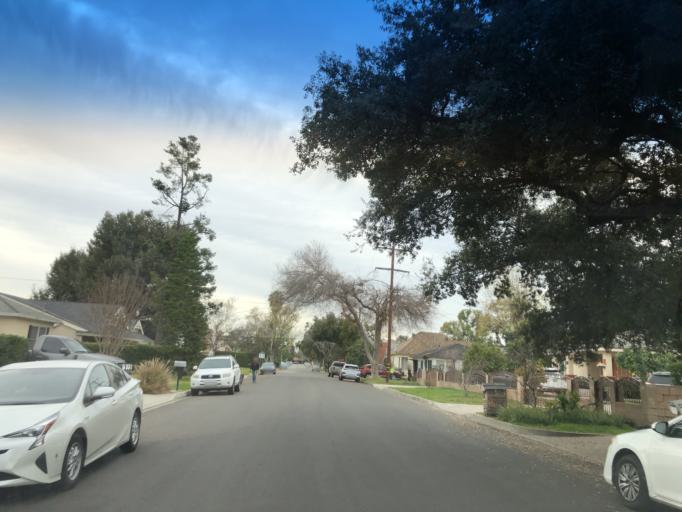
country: US
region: California
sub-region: Los Angeles County
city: Arcadia
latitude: 34.1358
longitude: -118.0194
